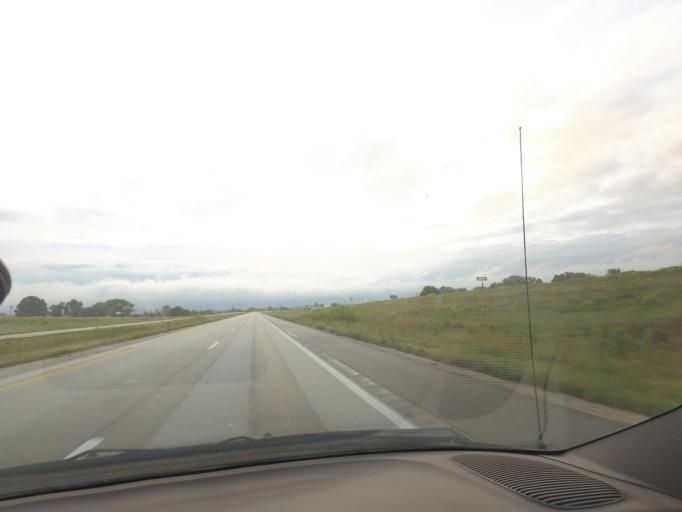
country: US
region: Missouri
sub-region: Shelby County
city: Shelbina
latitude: 39.6978
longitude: -92.0389
